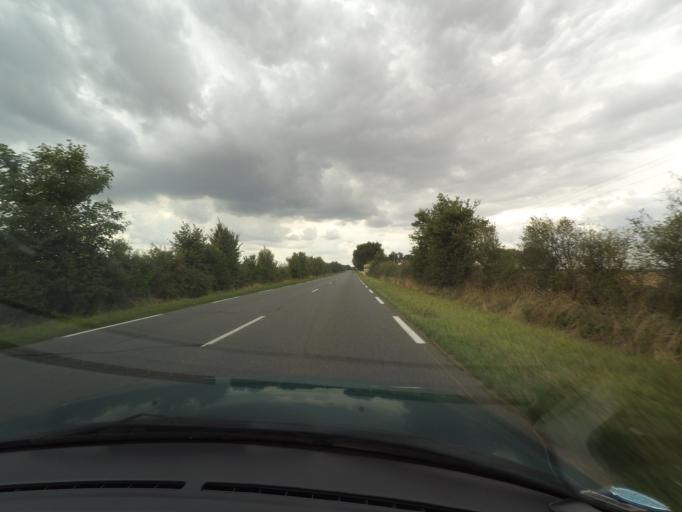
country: FR
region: Poitou-Charentes
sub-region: Departement de la Vienne
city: Ayron
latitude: 46.6566
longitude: 0.0998
